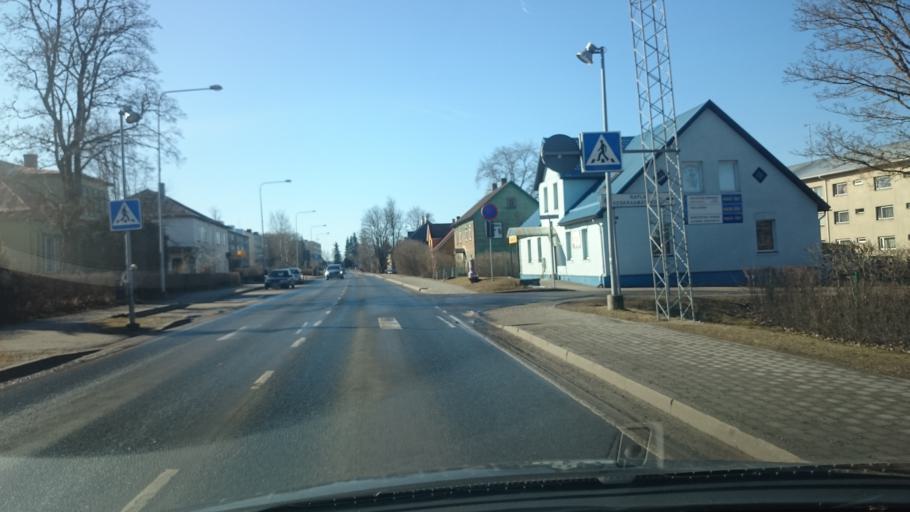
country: EE
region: Raplamaa
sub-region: Rapla vald
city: Rapla
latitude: 59.0023
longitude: 24.7928
